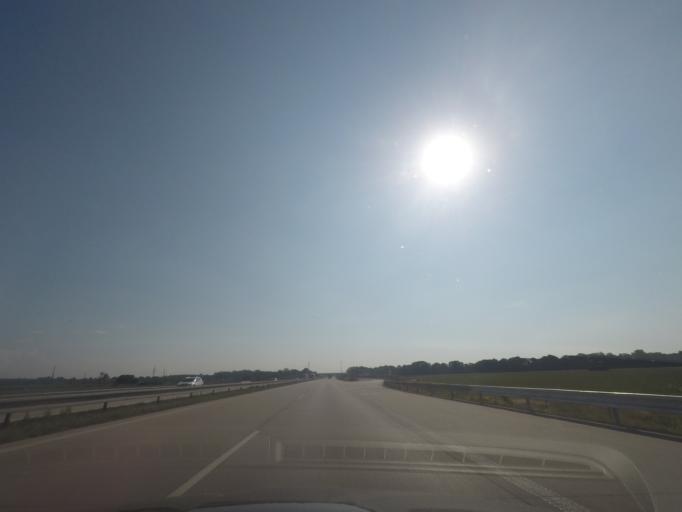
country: PL
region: Silesian Voivodeship
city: Gorzyczki
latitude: 49.9260
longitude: 18.3853
